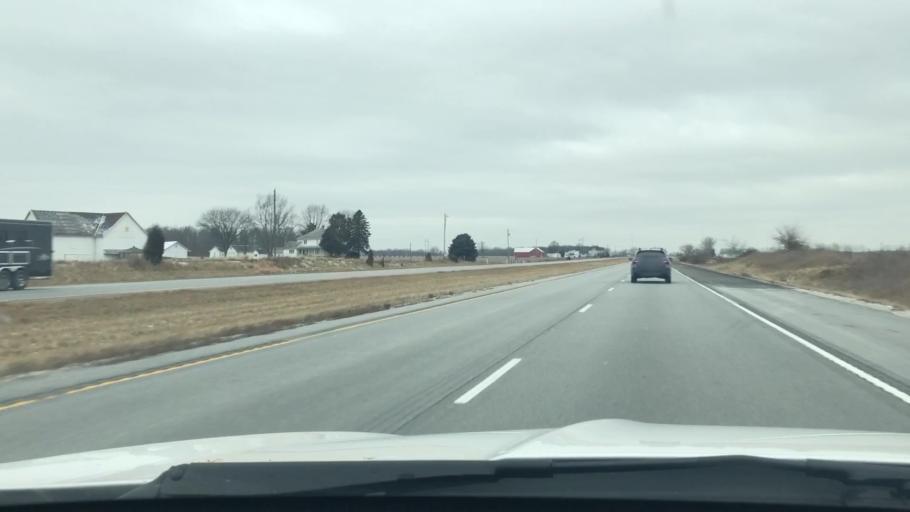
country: US
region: Indiana
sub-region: Miami County
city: Peru
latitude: 40.8585
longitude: -86.1332
